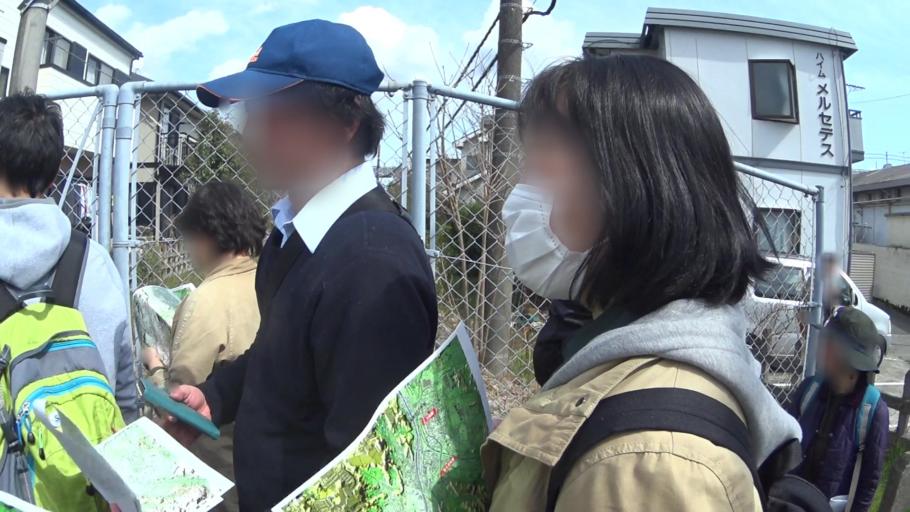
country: JP
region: Kanagawa
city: Kamakura
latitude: 35.3464
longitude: 139.5280
